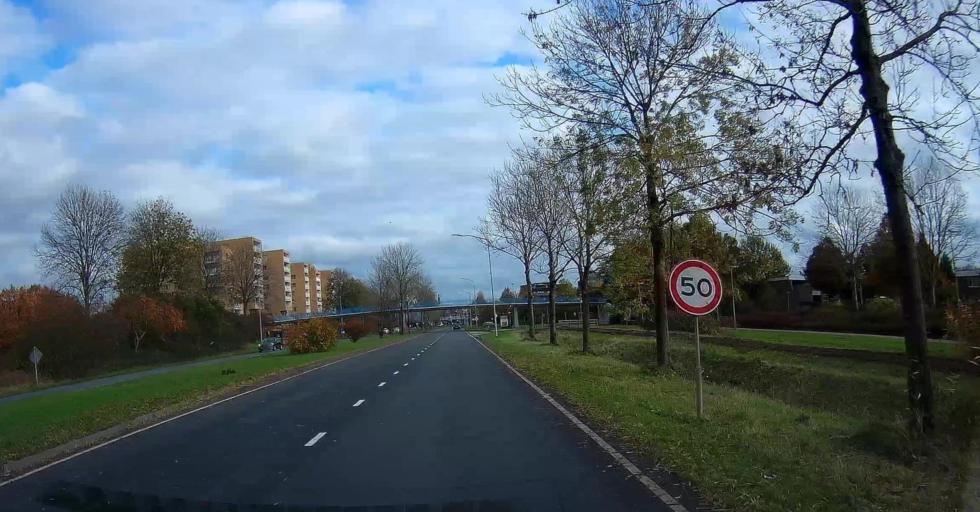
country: NL
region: Flevoland
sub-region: Gemeente Lelystad
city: Lelystad
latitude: 52.5071
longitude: 5.4649
